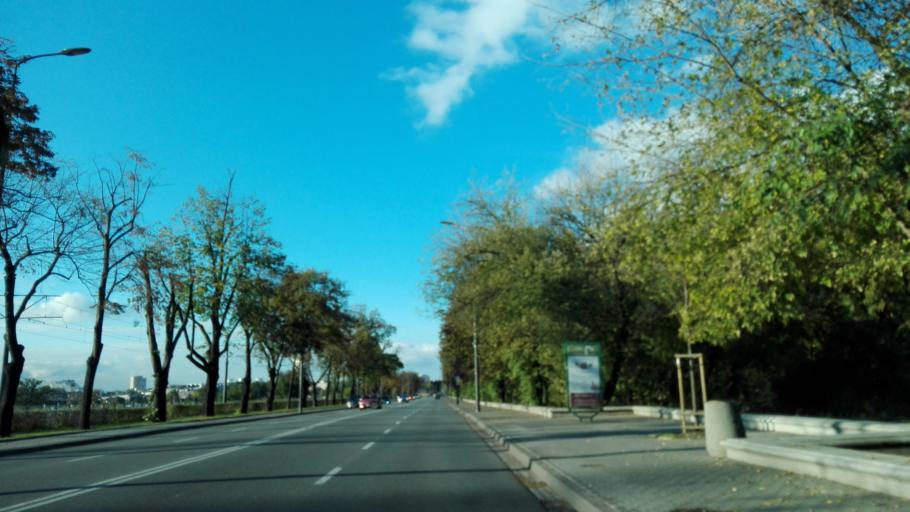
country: PL
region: Masovian Voivodeship
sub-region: Warszawa
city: Praga Polnoc
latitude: 52.2416
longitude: 21.0500
